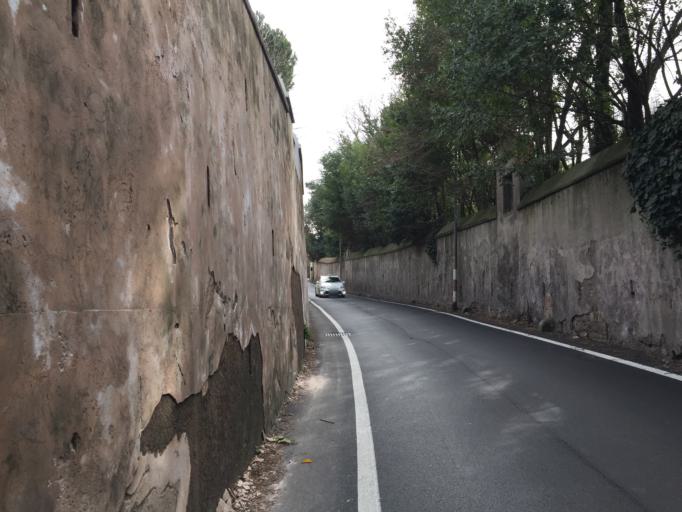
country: VA
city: Vatican City
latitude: 41.8885
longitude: 12.4582
